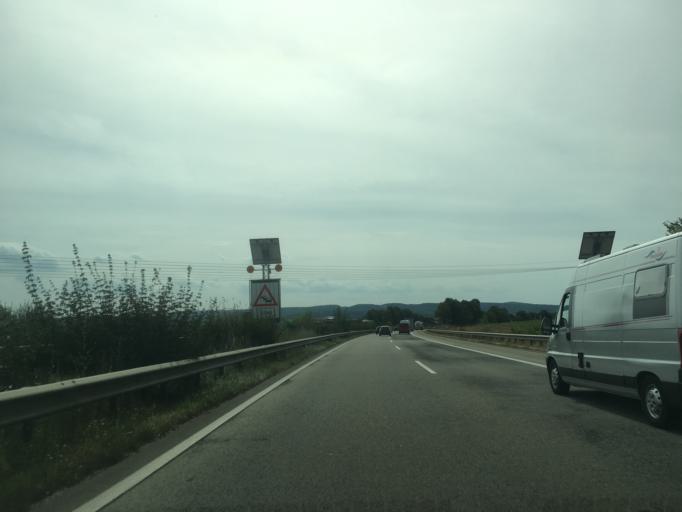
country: DE
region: Rheinland-Pfalz
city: Winningen
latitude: 50.3310
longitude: 7.5135
